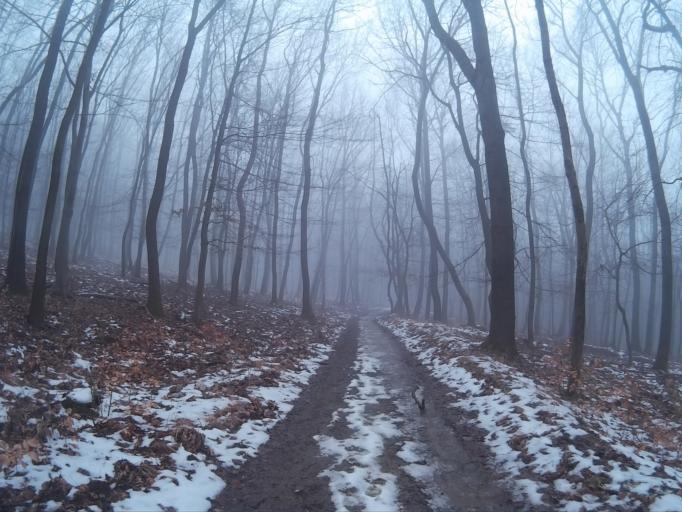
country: HU
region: Komarom-Esztergom
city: Tardos
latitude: 47.6837
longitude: 18.4745
